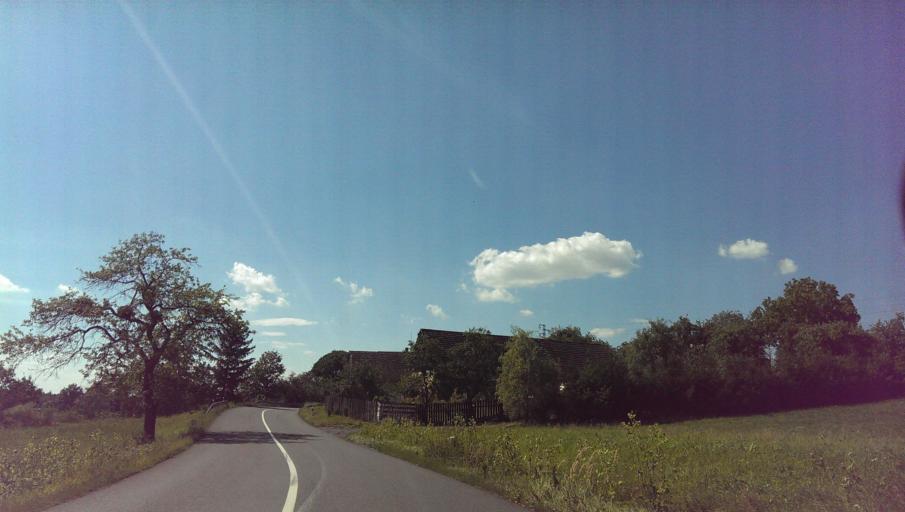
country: CZ
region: Zlin
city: Valasske Mezirici
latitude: 49.4631
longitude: 17.9249
